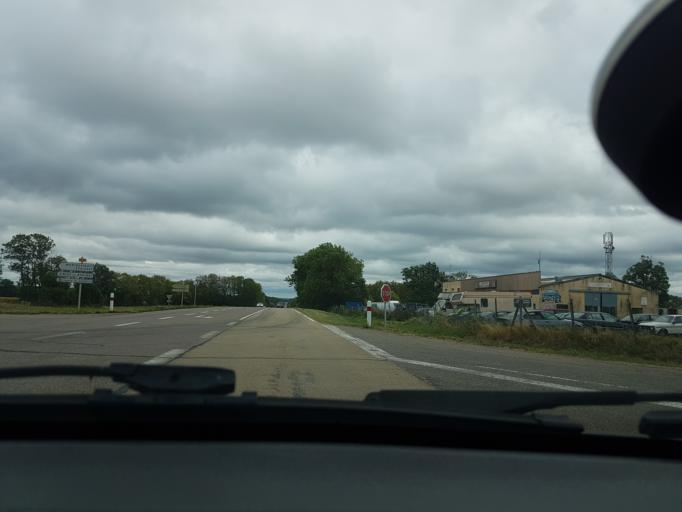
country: FR
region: Bourgogne
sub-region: Departement de la Cote-d'Or
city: Saulieu
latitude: 47.4254
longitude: 4.1133
